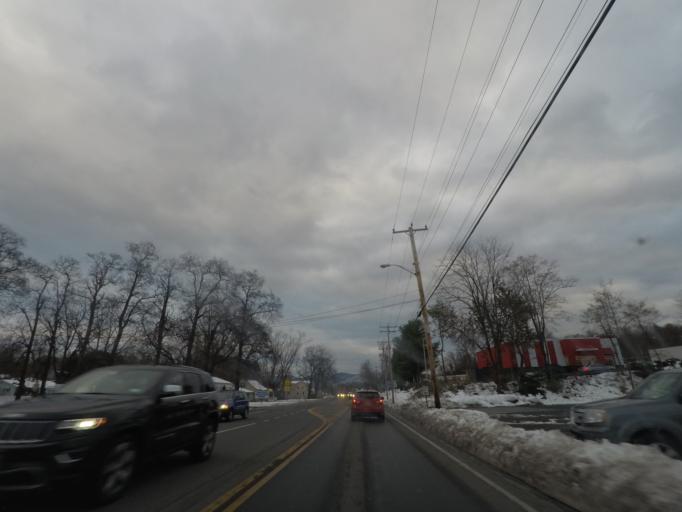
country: US
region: New York
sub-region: Orange County
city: Balmville
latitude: 41.5222
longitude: -74.0273
